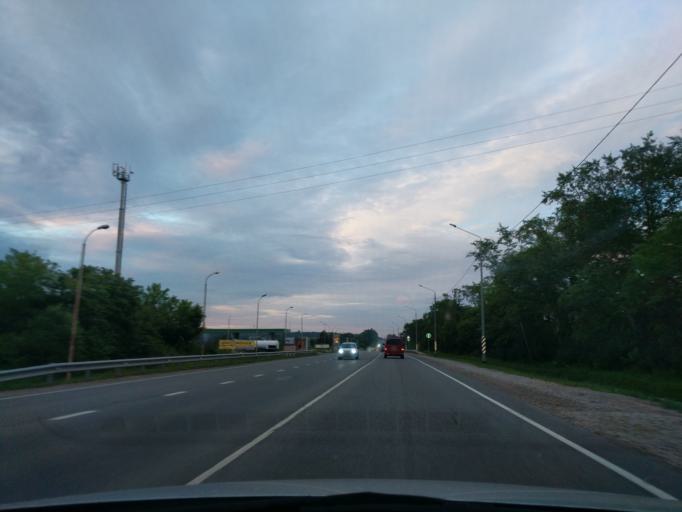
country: RU
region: Kaluga
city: Obninsk
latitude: 55.0685
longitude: 36.6056
